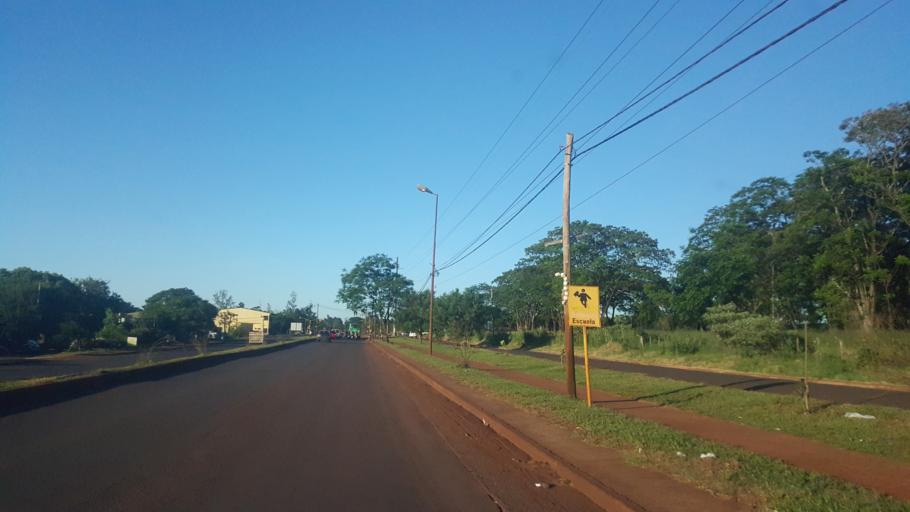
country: AR
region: Misiones
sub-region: Departamento de Capital
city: Posadas
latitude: -27.4236
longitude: -55.9331
